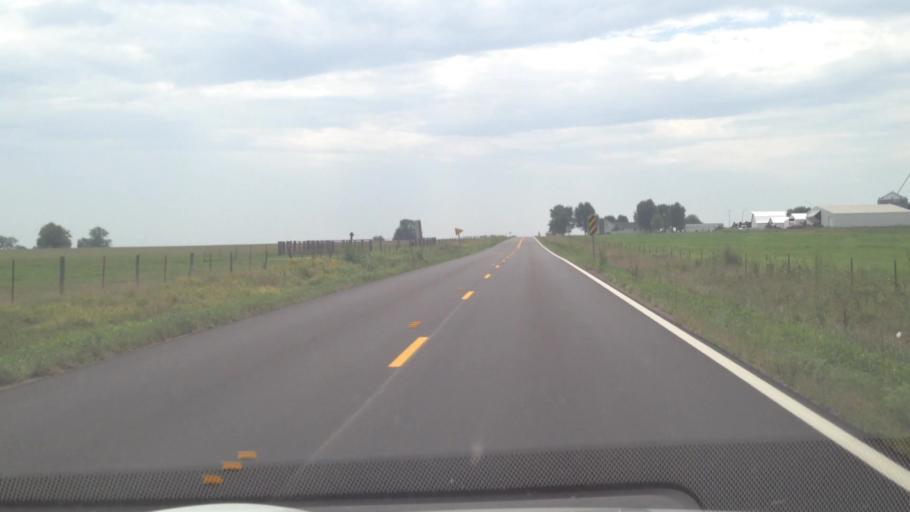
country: US
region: Kansas
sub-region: Crawford County
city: Girard
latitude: 37.5497
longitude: -94.9605
